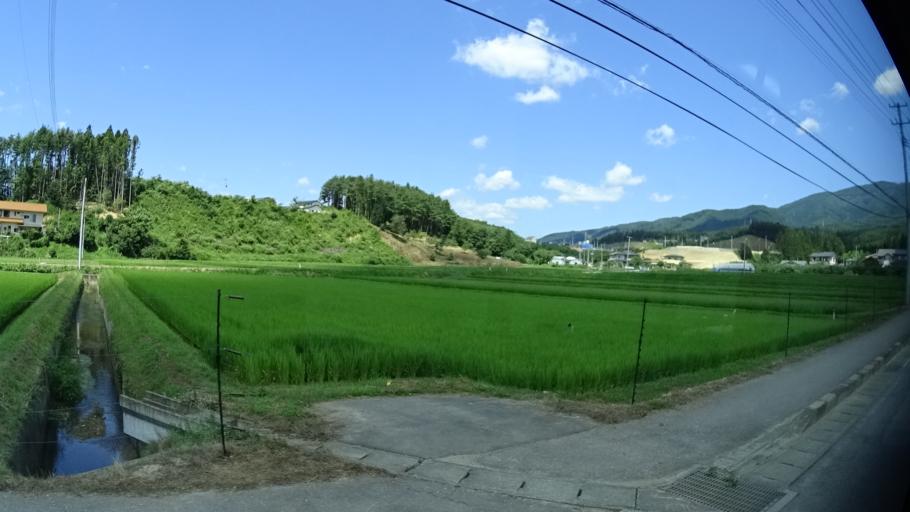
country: JP
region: Iwate
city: Ofunato
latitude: 39.0190
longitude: 141.6464
